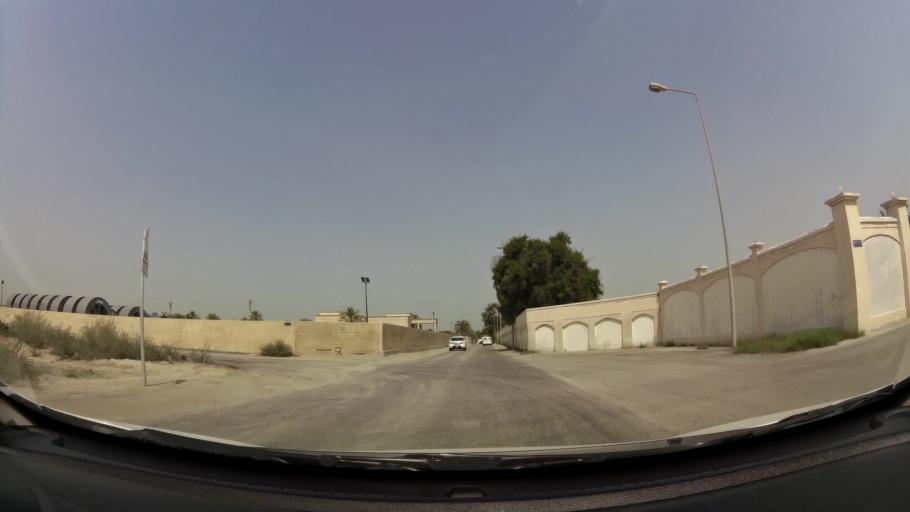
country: BH
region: Manama
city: Jidd Hafs
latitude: 26.2217
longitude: 50.4781
